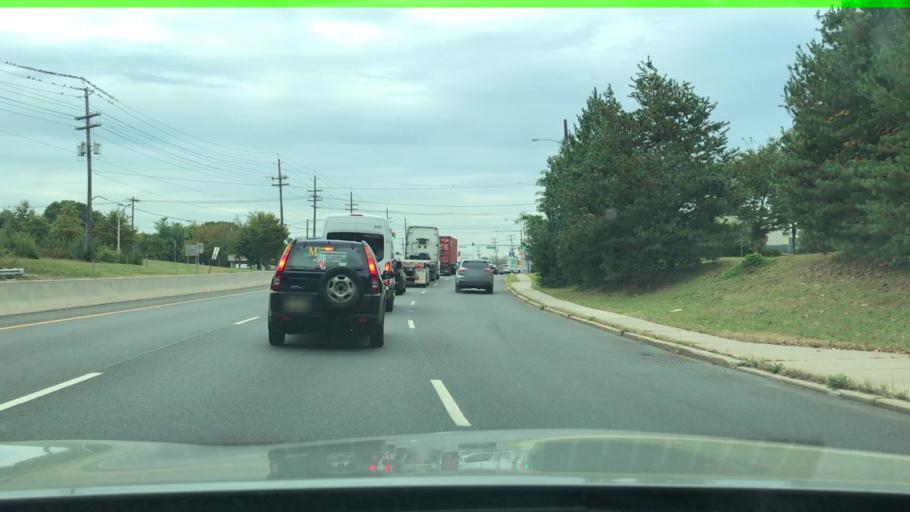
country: US
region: New Jersey
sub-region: Somerset County
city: Raritan
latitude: 40.5709
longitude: -74.6260
